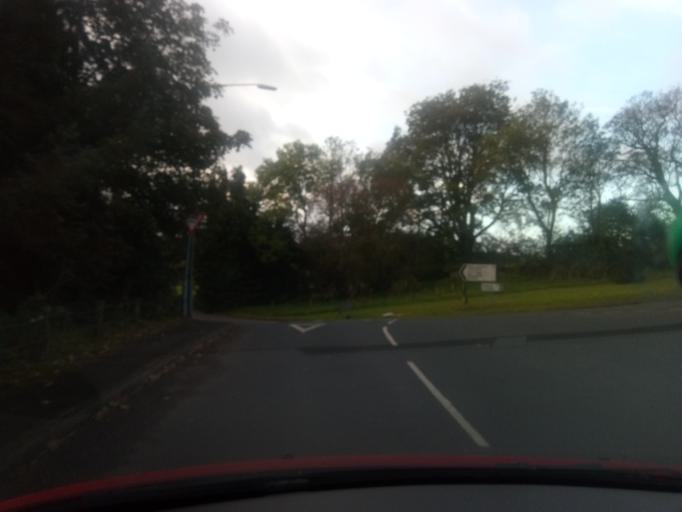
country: GB
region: Scotland
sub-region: The Scottish Borders
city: Jedburgh
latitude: 55.4019
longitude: -2.6561
